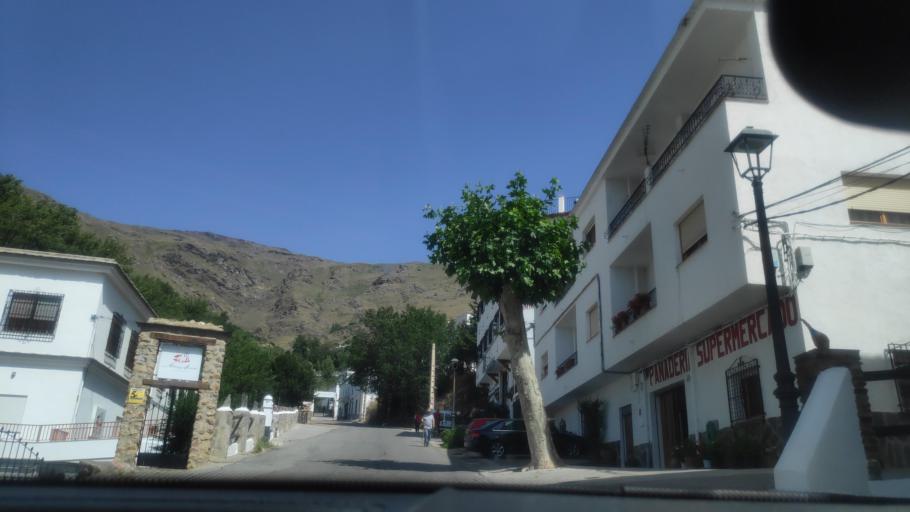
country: ES
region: Andalusia
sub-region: Provincia de Granada
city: Trevelez
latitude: 36.9996
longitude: -3.2655
